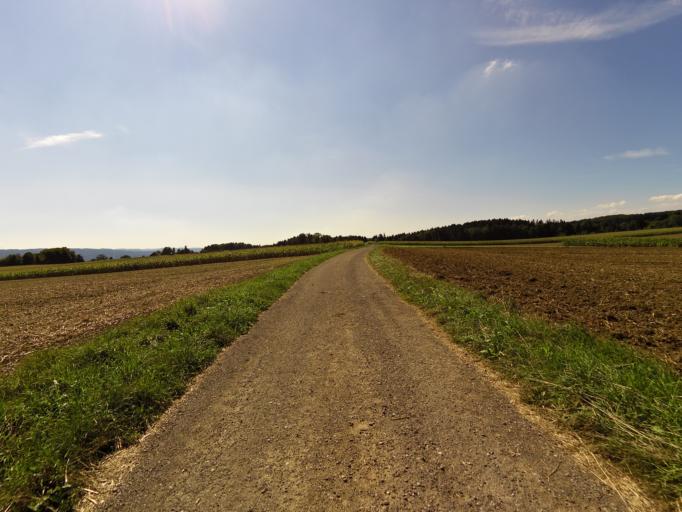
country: CH
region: Thurgau
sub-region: Weinfelden District
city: Wigoltingen
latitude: 47.6275
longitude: 9.0455
